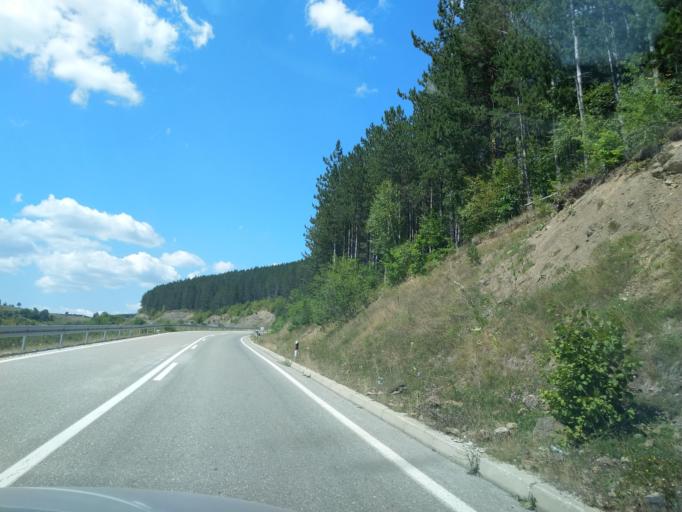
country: RS
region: Central Serbia
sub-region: Zlatiborski Okrug
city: Sjenica
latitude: 43.2997
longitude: 19.9357
